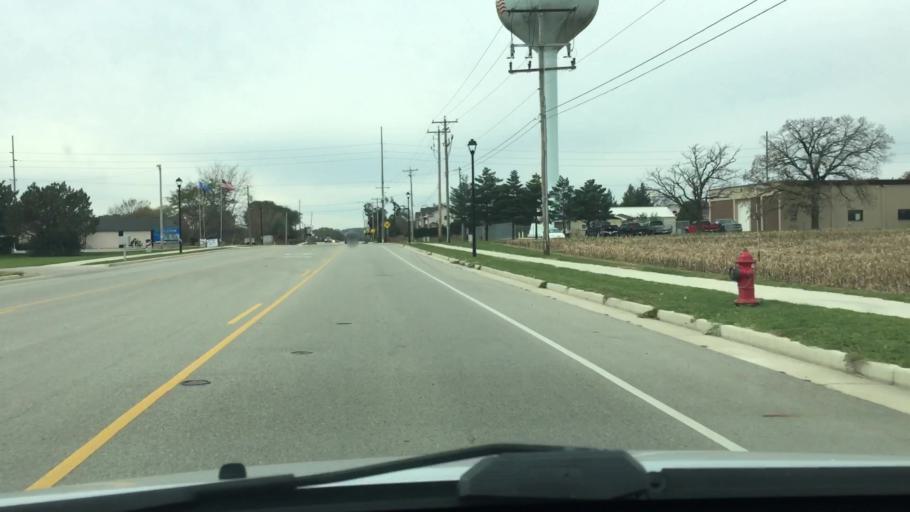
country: US
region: Wisconsin
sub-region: Waukesha County
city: Mukwonago
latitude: 42.8737
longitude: -88.3247
